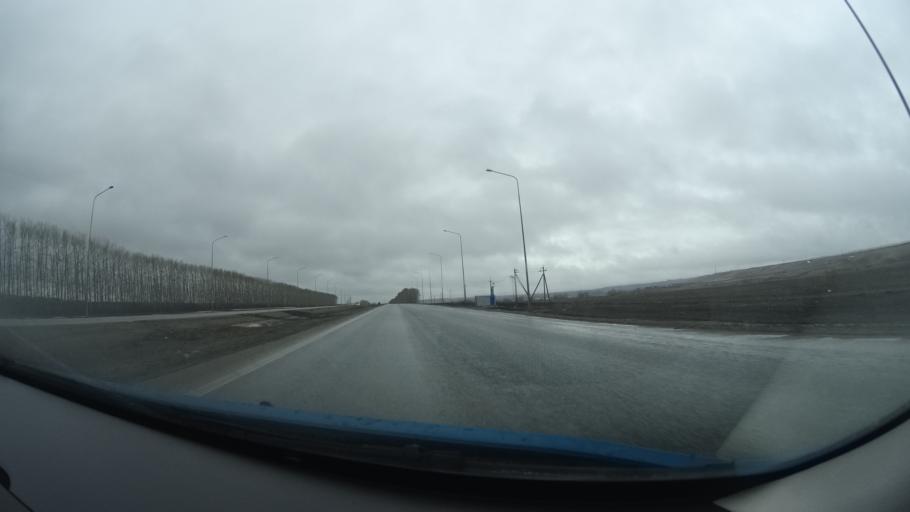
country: RU
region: Bashkortostan
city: Alekseyevka
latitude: 54.7282
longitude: 54.9603
